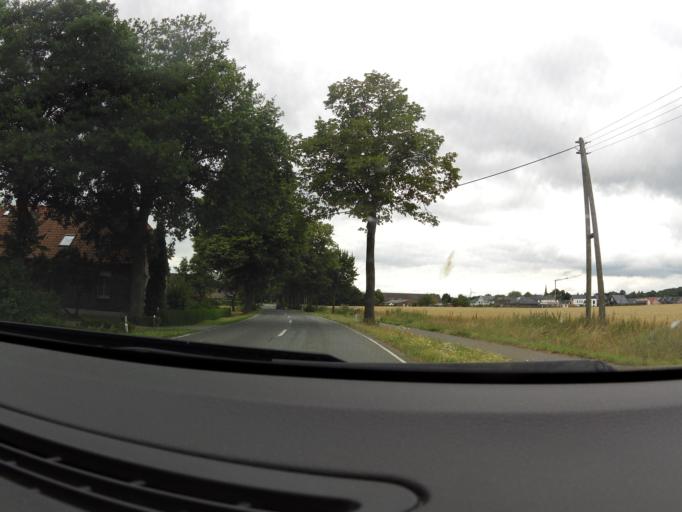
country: DE
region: North Rhine-Westphalia
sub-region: Regierungsbezirk Dusseldorf
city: Sonsbeck
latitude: 51.6114
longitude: 6.3878
